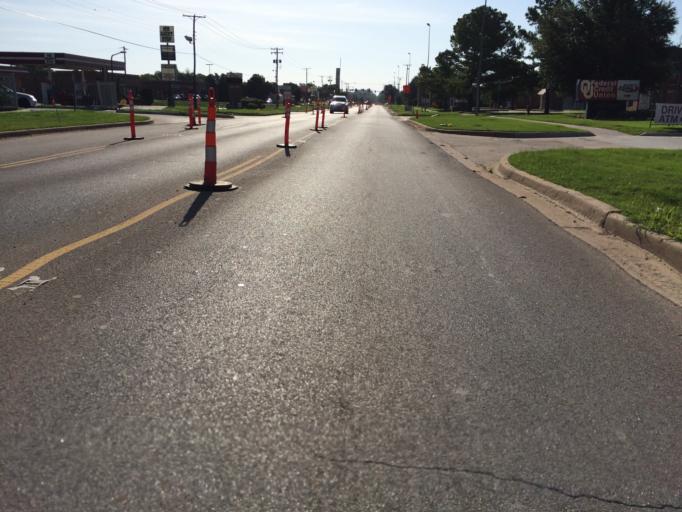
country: US
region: Oklahoma
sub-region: Cleveland County
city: Norman
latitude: 35.2039
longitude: -97.4714
